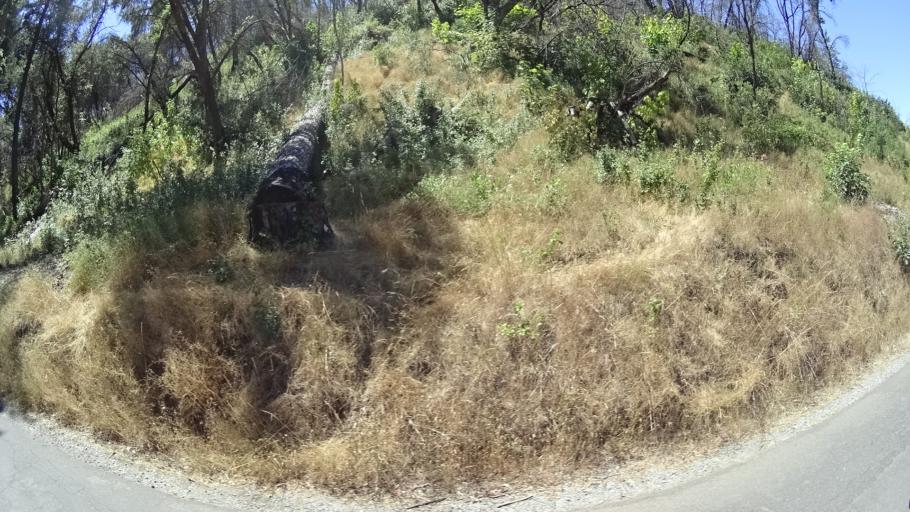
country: US
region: California
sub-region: Calaveras County
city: Mountain Ranch
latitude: 38.1950
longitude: -120.5751
